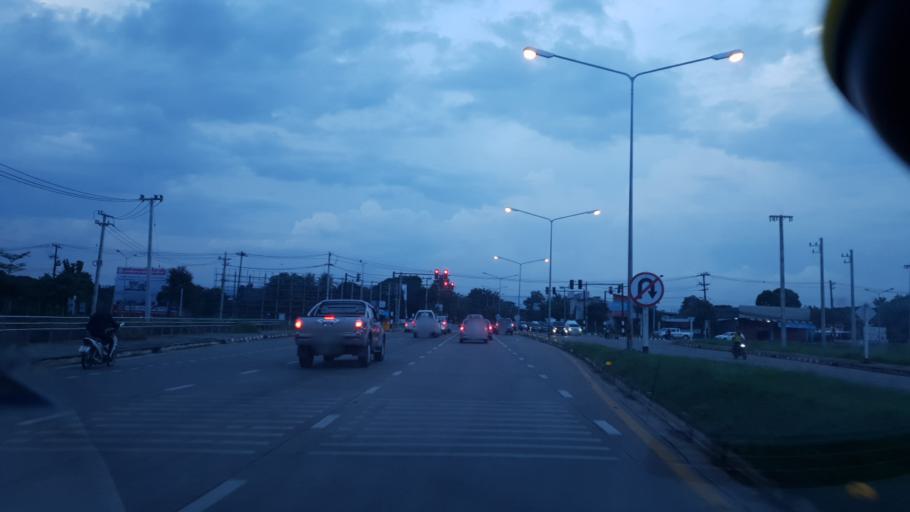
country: TH
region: Chiang Rai
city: Chiang Rai
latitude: 19.9080
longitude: 99.8597
